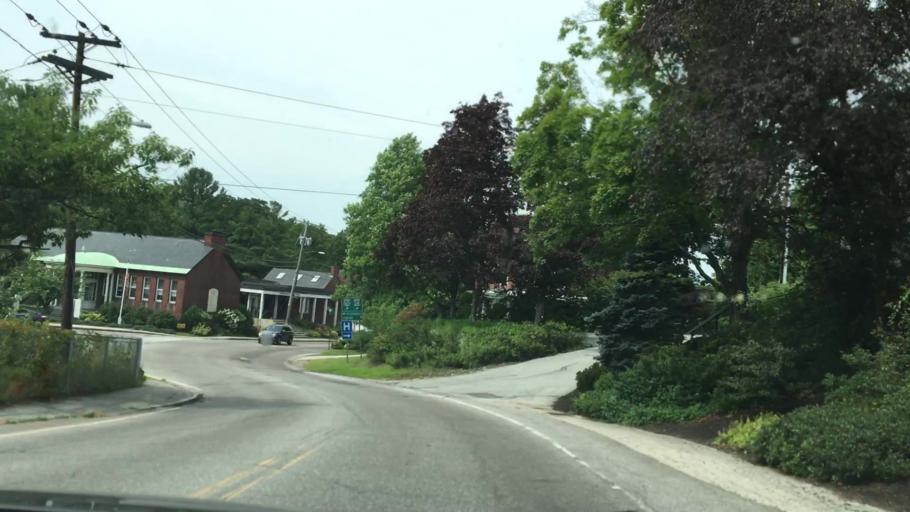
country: US
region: New Hampshire
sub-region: Hillsborough County
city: Peterborough
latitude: 42.8770
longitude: -71.9477
